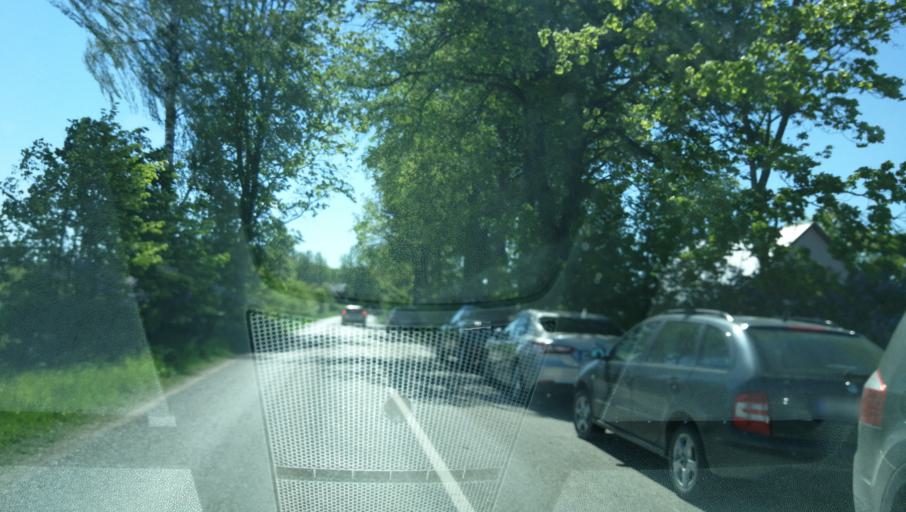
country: LV
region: Dobeles Rajons
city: Dobele
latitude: 56.6064
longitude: 23.2997
